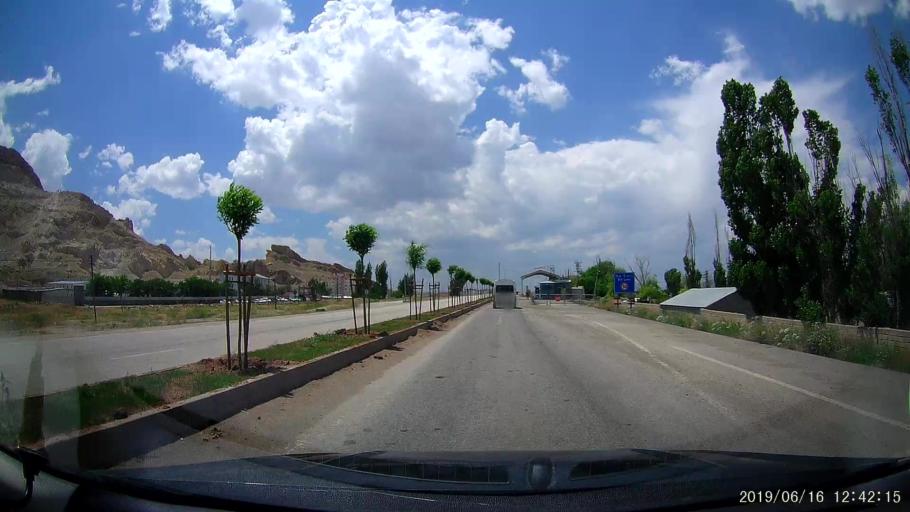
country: TR
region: Agri
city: Dogubayazit
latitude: 39.5583
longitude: 44.1252
